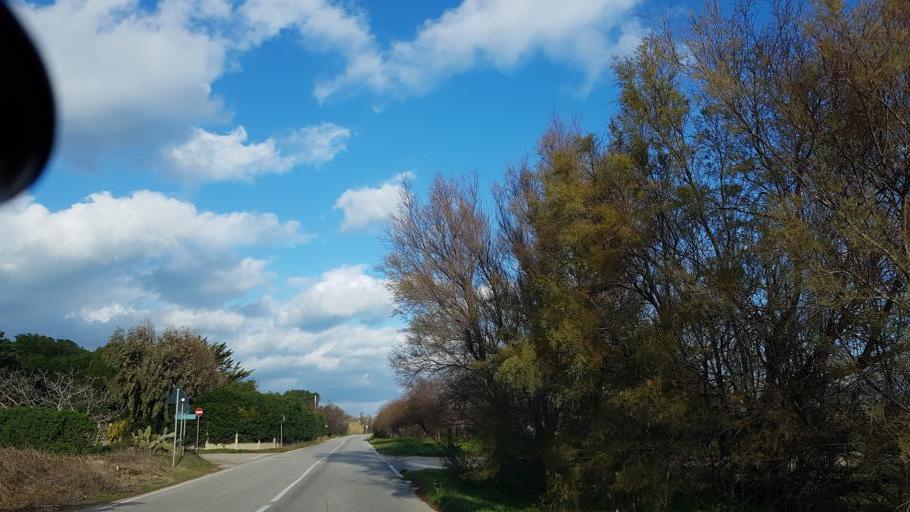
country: IT
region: Apulia
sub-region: Provincia di Brindisi
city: Materdomini
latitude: 40.6682
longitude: 17.9479
